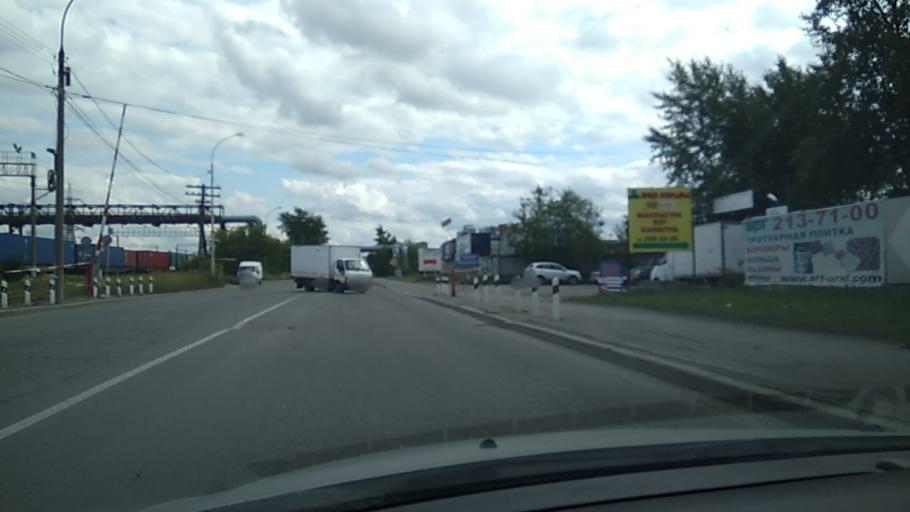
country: RU
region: Sverdlovsk
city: Yekaterinburg
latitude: 56.8806
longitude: 60.5484
